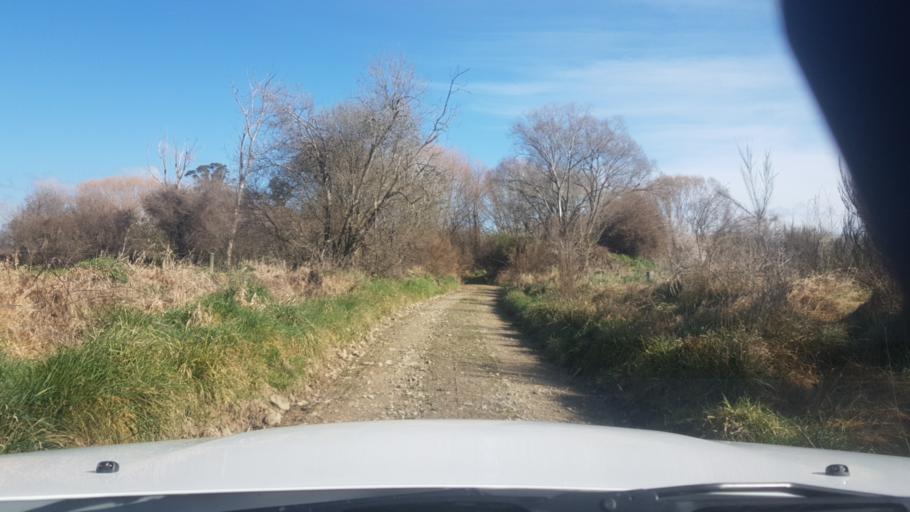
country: NZ
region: Canterbury
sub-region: Timaru District
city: Pleasant Point
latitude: -44.1716
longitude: 171.2358
